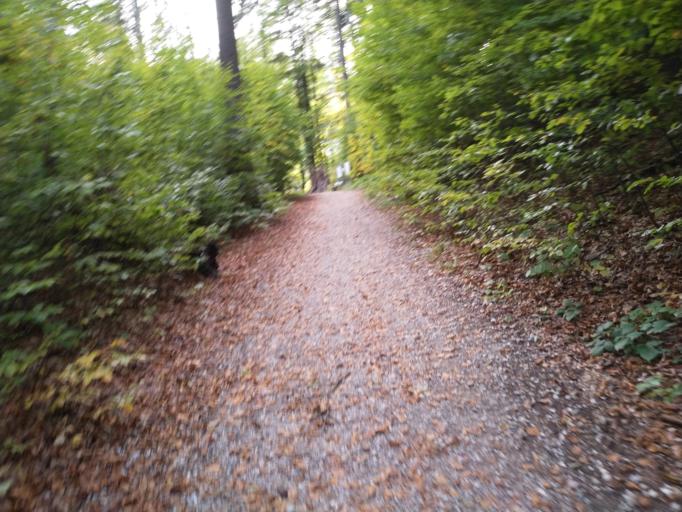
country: AT
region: Tyrol
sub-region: Politischer Bezirk Reutte
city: Vils
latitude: 47.5594
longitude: 10.6383
